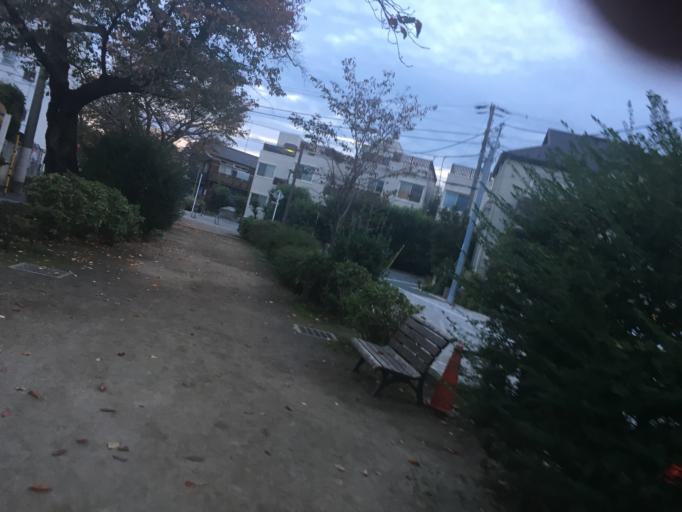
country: JP
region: Tokyo
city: Tokyo
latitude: 35.6167
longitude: 139.6613
